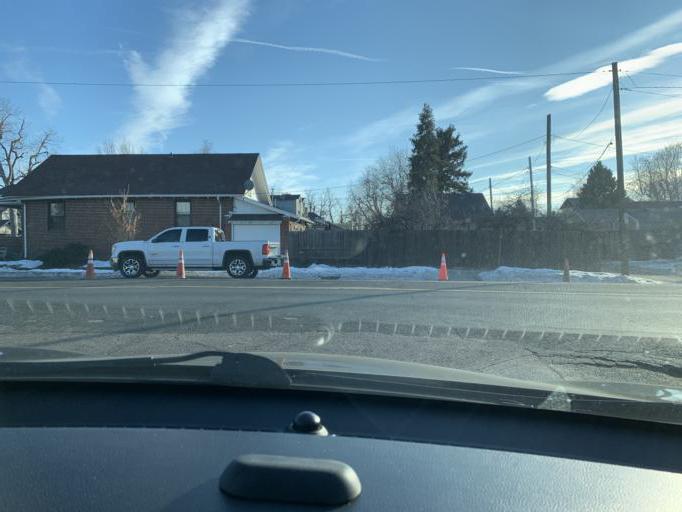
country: US
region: Colorado
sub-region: Adams County
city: Berkley
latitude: 39.7769
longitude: -105.0315
